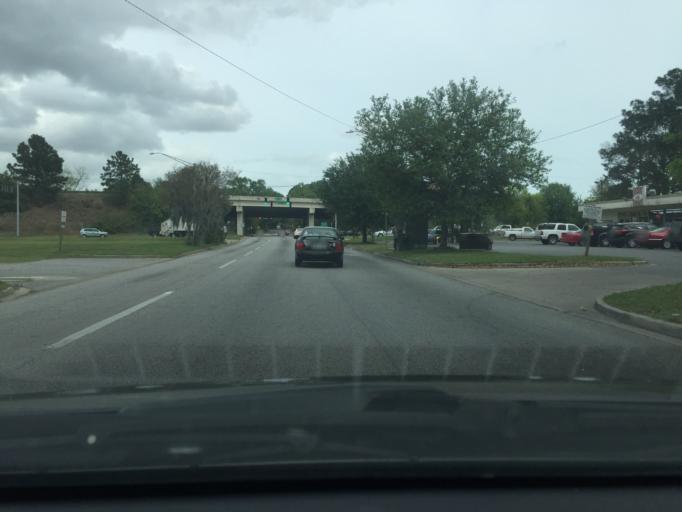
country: US
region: Georgia
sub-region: Chatham County
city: Thunderbolt
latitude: 32.0560
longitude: -81.0742
